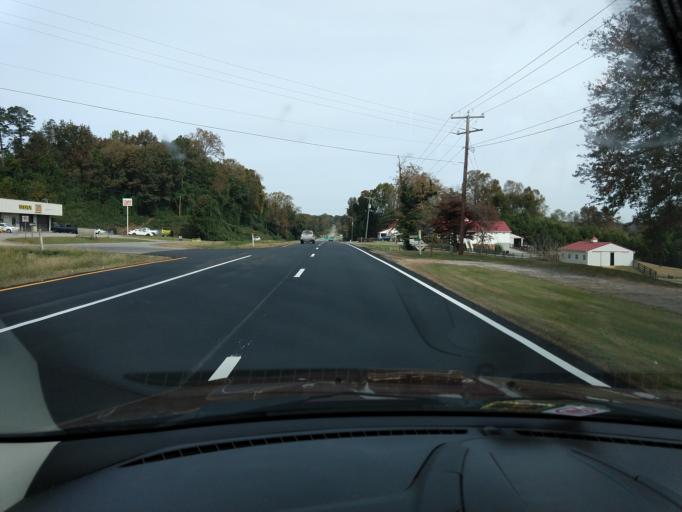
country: US
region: Virginia
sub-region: Pittsylvania County
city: Chatham
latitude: 36.7980
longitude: -79.3934
